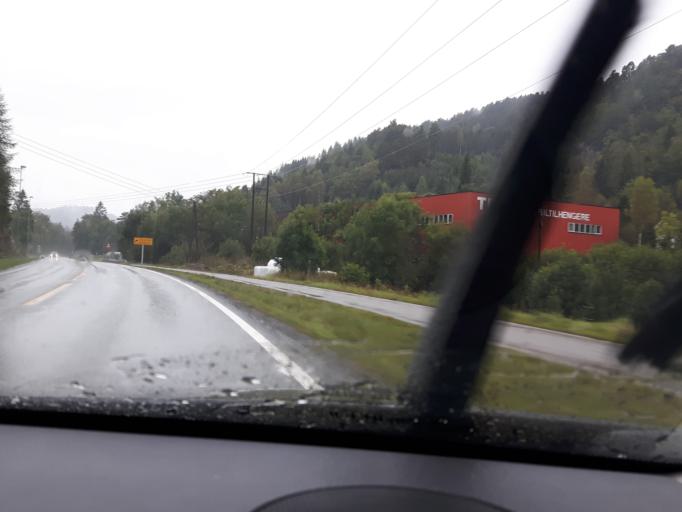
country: NO
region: Vest-Agder
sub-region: Lindesnes
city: Vigeland
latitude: 58.0754
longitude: 7.3375
